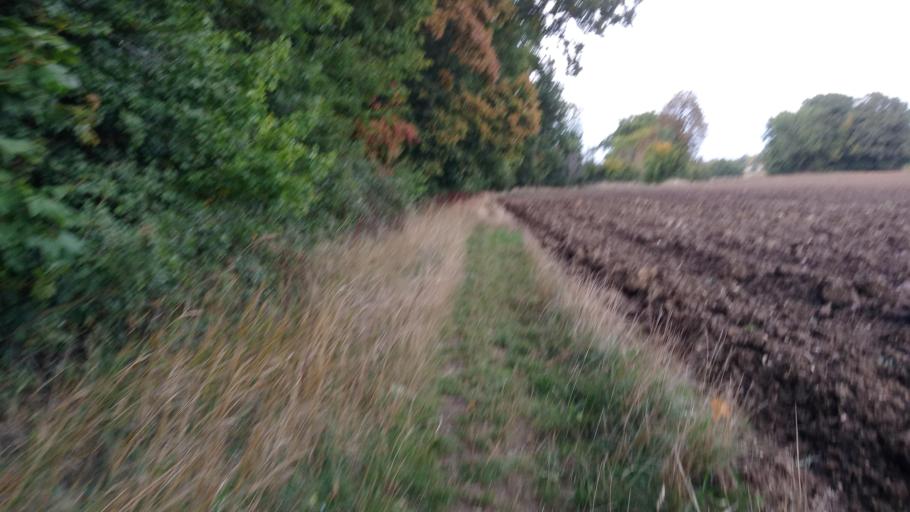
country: GB
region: England
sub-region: Cambridgeshire
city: Linton
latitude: 52.0555
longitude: 0.3085
